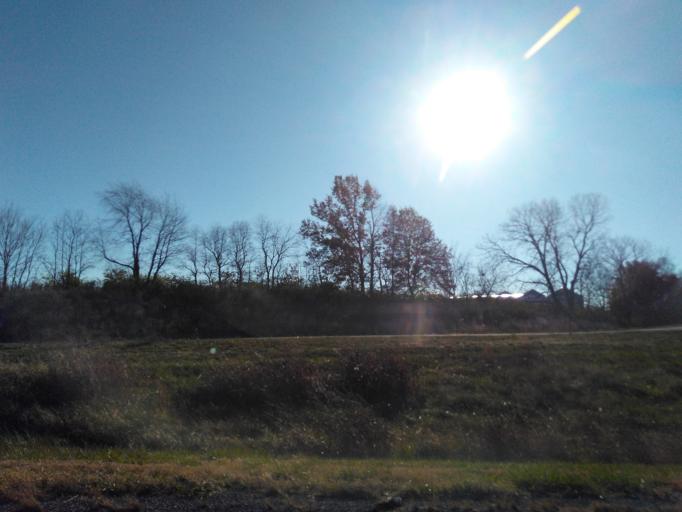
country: US
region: Illinois
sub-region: Madison County
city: Saint Jacob
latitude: 38.7781
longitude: -89.7409
